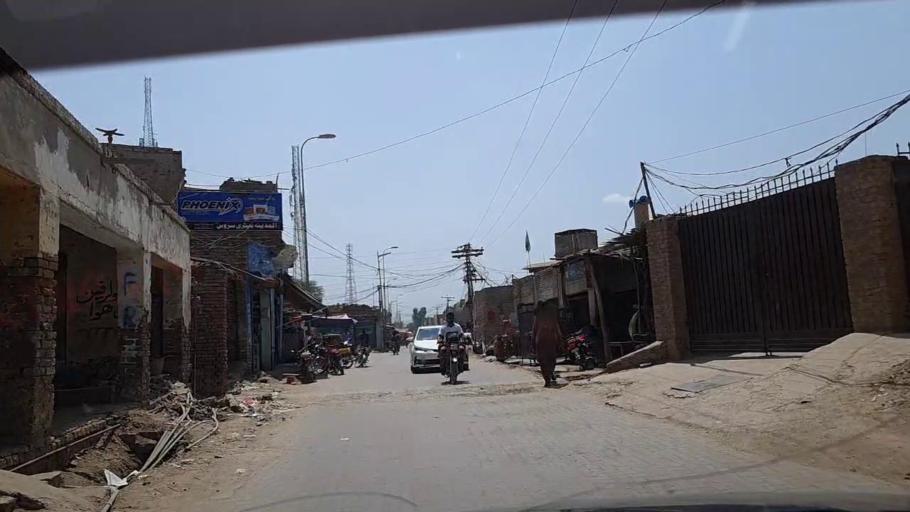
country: PK
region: Sindh
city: Khanpur
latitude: 27.8414
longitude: 69.4124
